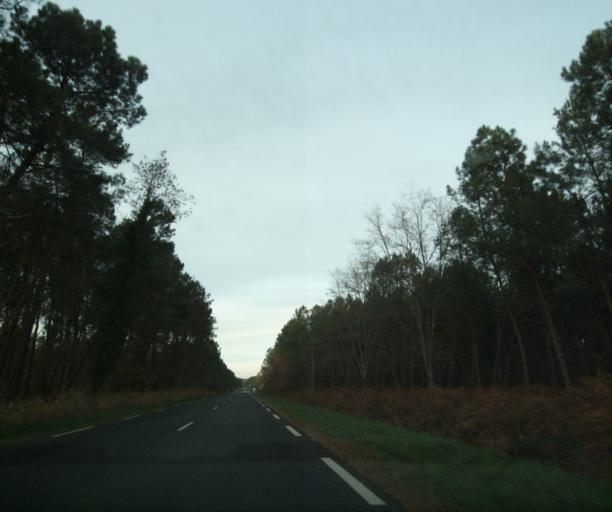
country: FR
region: Aquitaine
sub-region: Departement de la Gironde
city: Bazas
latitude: 44.3426
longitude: -0.2353
